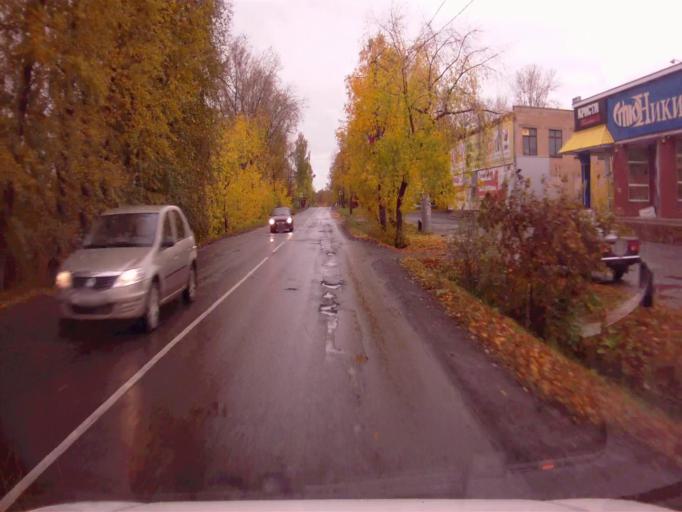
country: RU
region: Chelyabinsk
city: Verkhniy Ufaley
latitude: 56.0395
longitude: 60.2537
